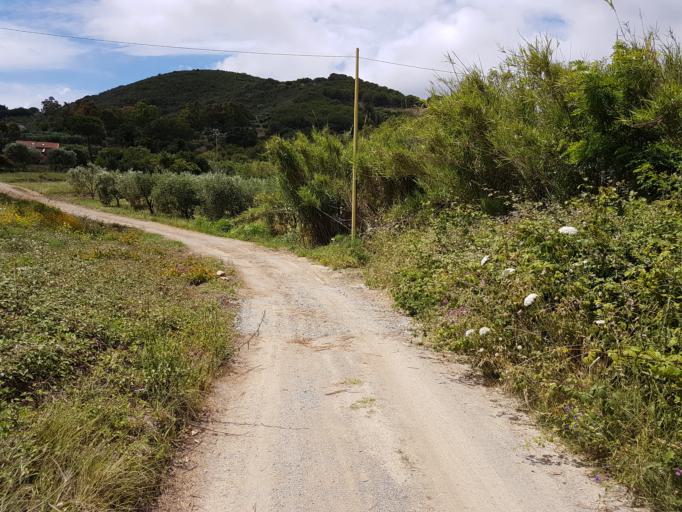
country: IT
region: Tuscany
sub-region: Provincia di Livorno
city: Capoliveri
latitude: 42.7725
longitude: 10.3473
